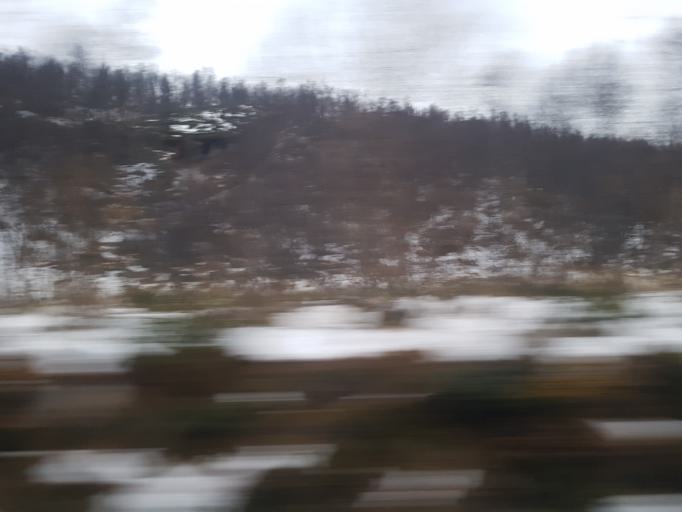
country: NO
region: Sor-Trondelag
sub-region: Oppdal
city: Oppdal
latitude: 62.3001
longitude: 9.6022
